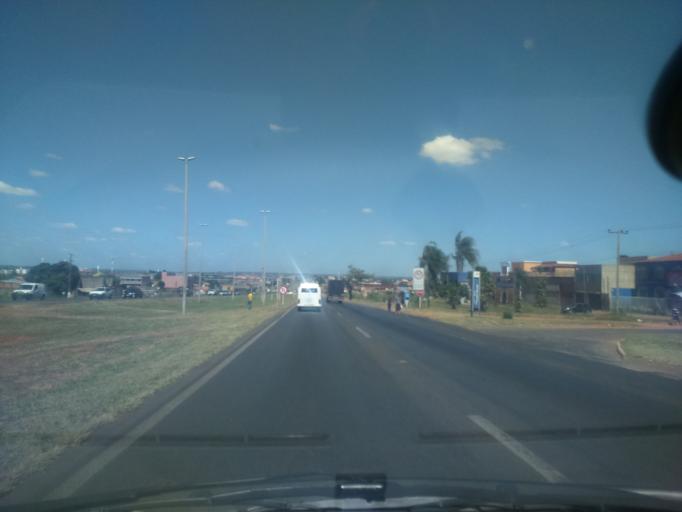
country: BR
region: Goias
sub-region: Luziania
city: Luziania
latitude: -16.1059
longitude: -47.9741
